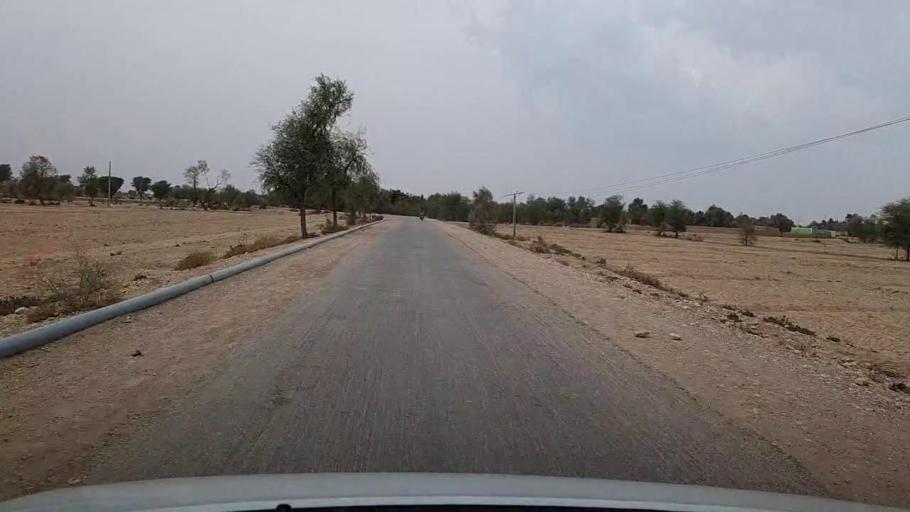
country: PK
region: Sindh
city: Sehwan
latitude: 26.3210
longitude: 67.7319
